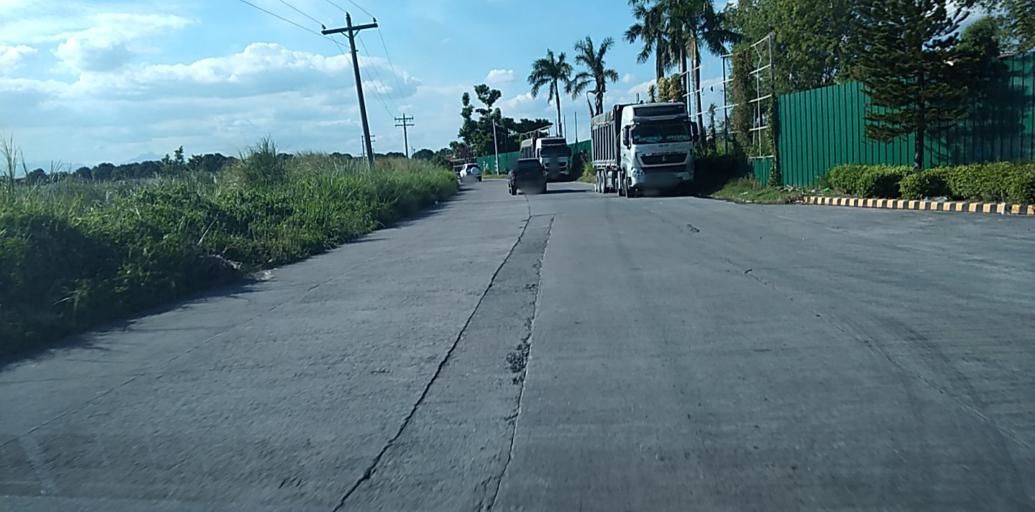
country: PH
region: Central Luzon
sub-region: Province of Pampanga
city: Acli
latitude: 15.1095
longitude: 120.6530
